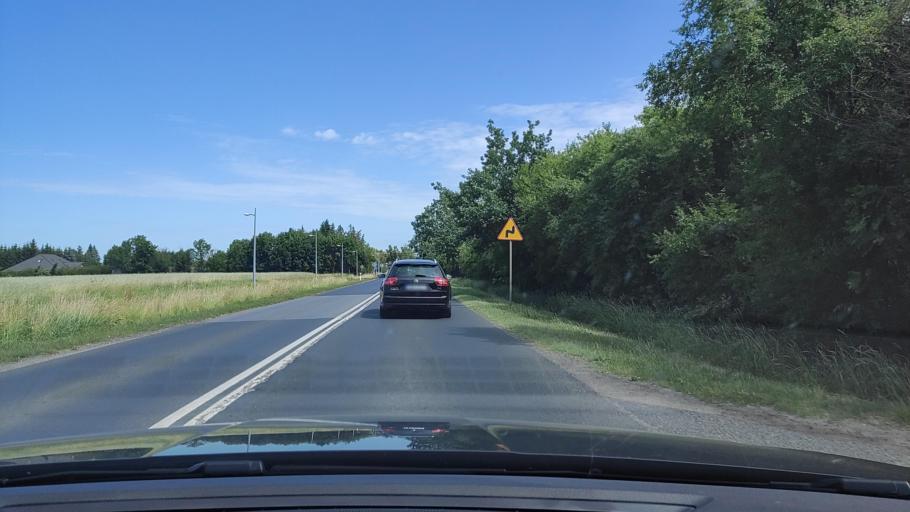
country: PL
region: Greater Poland Voivodeship
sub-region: Powiat poznanski
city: Czerwonak
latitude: 52.5045
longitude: 16.9758
